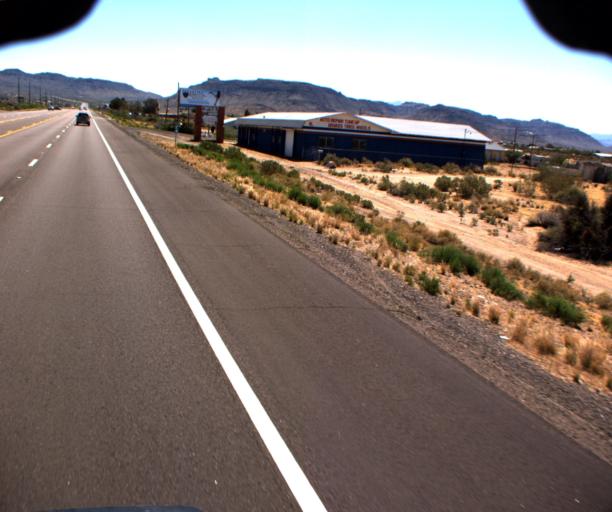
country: US
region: Arizona
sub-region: Mohave County
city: Golden Valley
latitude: 35.2202
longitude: -114.1804
